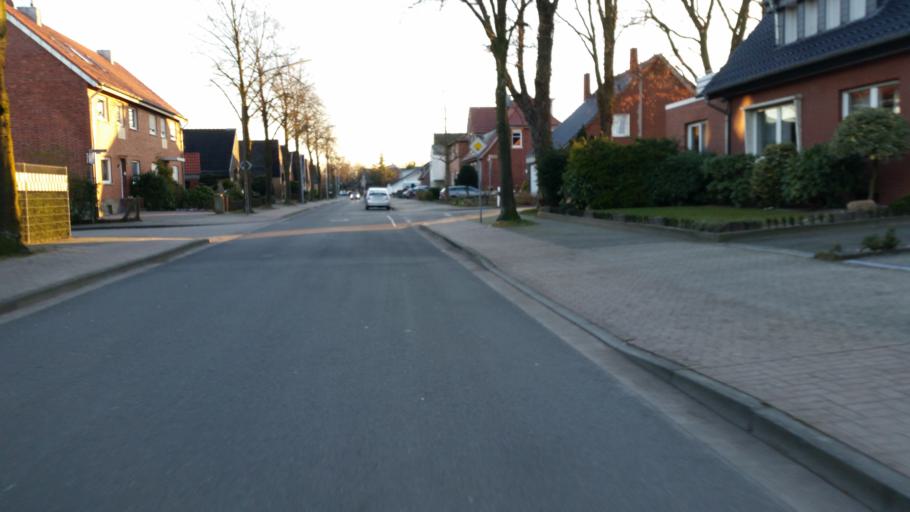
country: DE
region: North Rhine-Westphalia
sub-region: Regierungsbezirk Munster
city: Rheine
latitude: 52.2844
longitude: 7.4087
